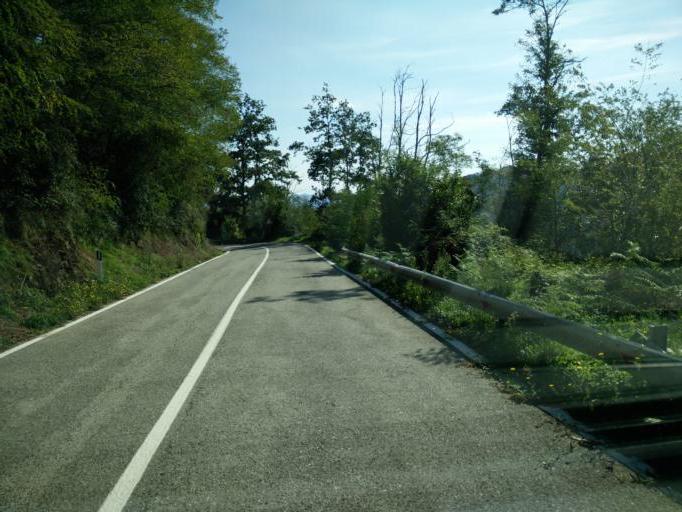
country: IT
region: Liguria
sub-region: Provincia di La Spezia
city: Carrodano
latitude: 44.2454
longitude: 9.6336
